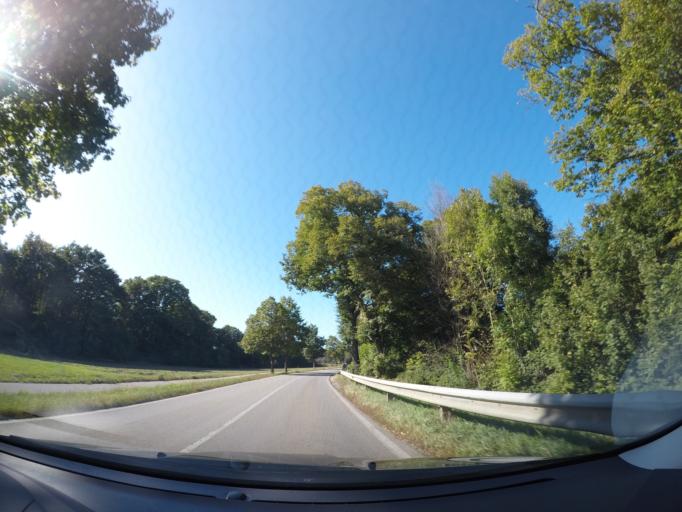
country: AT
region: Lower Austria
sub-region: Politischer Bezirk Modling
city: Laab im Walde
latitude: 48.1497
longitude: 16.1891
